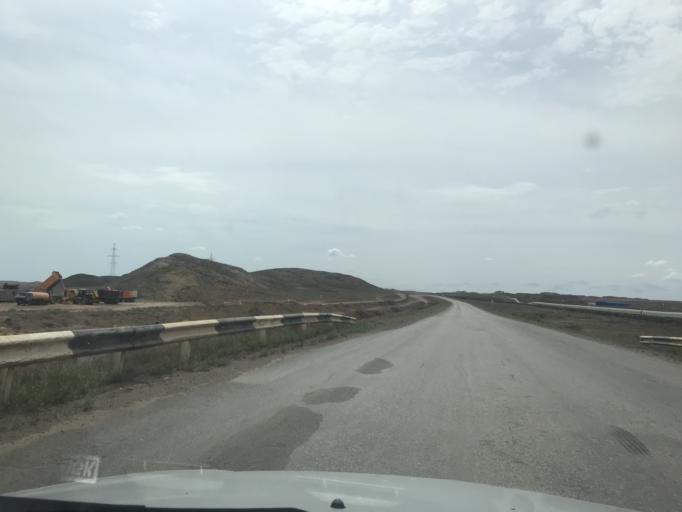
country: KZ
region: Zhambyl
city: Mynaral
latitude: 45.3741
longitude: 73.6562
